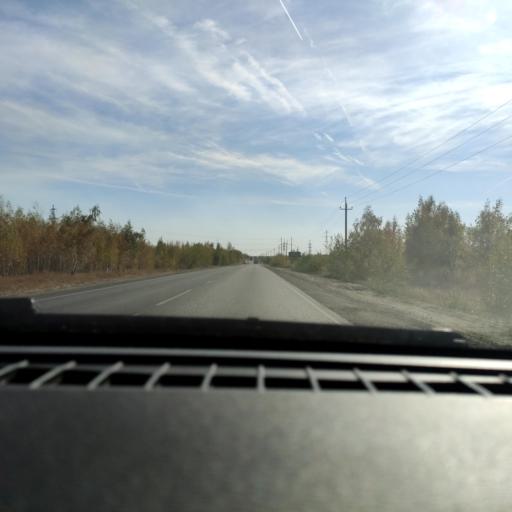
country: RU
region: Voronezj
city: Maslovka
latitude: 51.5859
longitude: 39.2558
